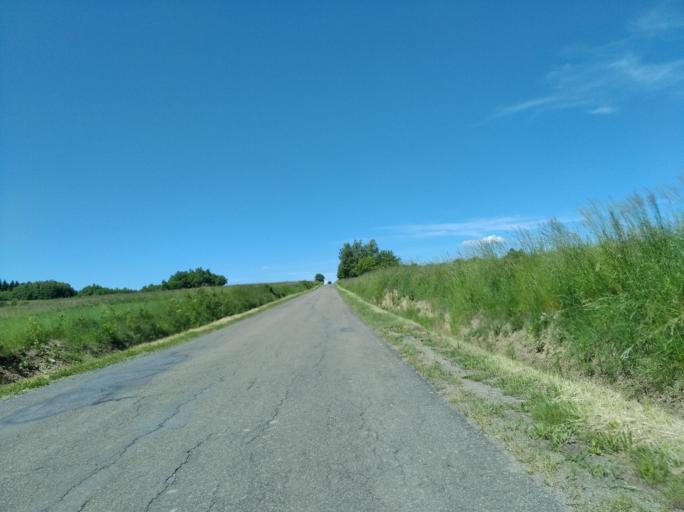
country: PL
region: Subcarpathian Voivodeship
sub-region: Powiat krosnienski
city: Chorkowka
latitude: 49.6407
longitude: 21.6296
